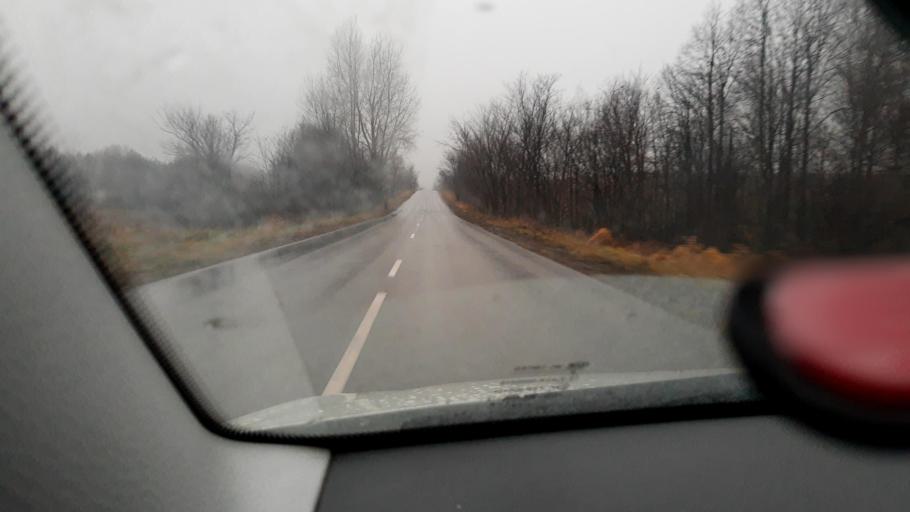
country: RU
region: Bashkortostan
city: Iglino
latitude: 54.8995
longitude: 56.2510
